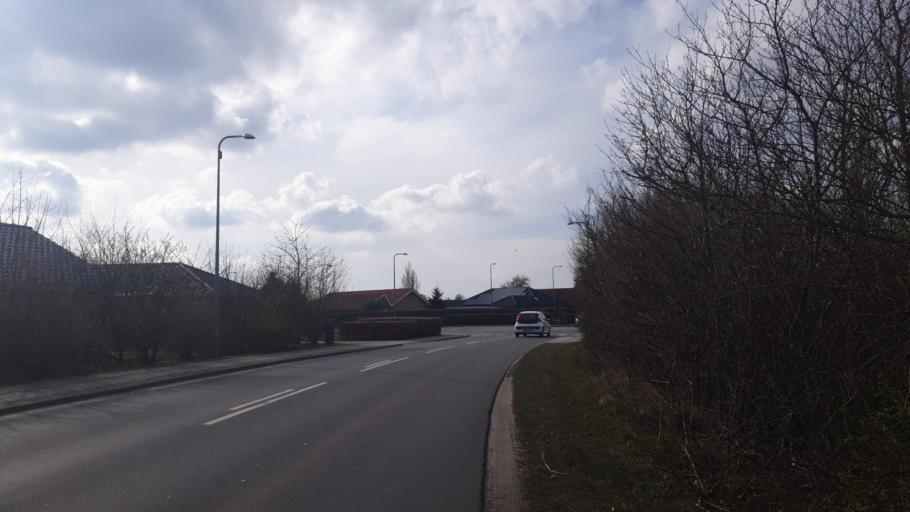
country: DK
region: Central Jutland
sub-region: Hedensted Kommune
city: Hedensted
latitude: 55.7658
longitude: 9.7120
